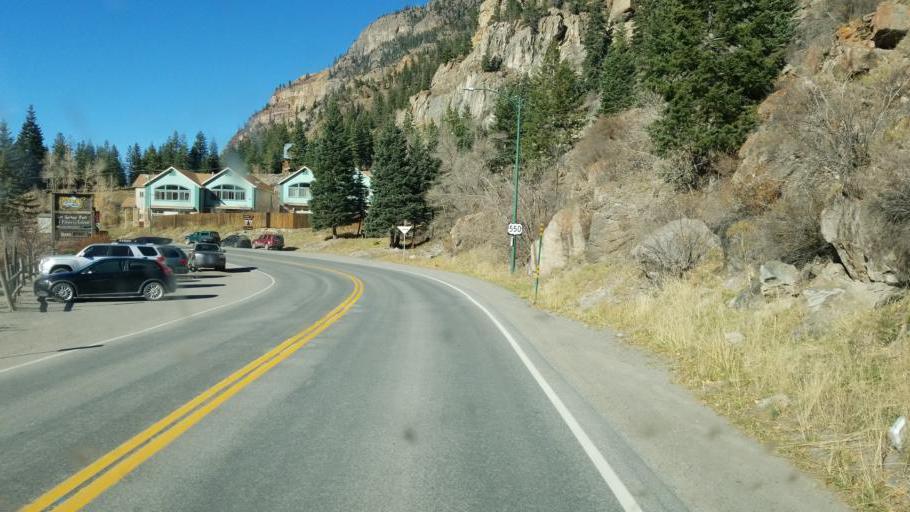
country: US
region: Colorado
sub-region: Ouray County
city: Ouray
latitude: 38.0288
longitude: -107.6715
